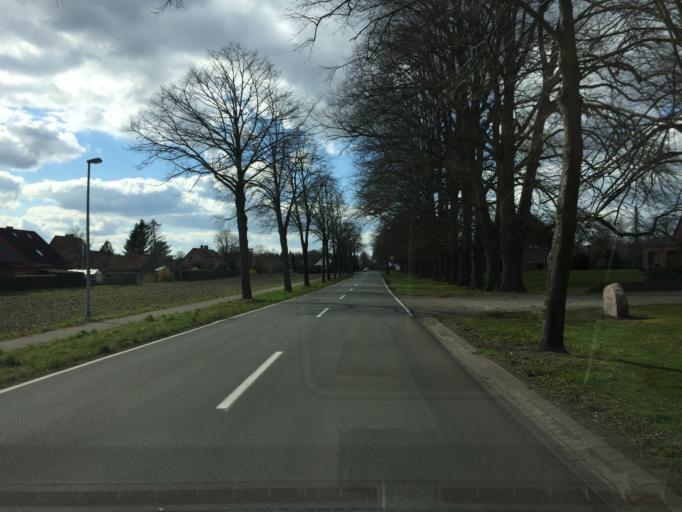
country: DE
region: Lower Saxony
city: Mellinghausen
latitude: 52.7076
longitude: 8.9057
